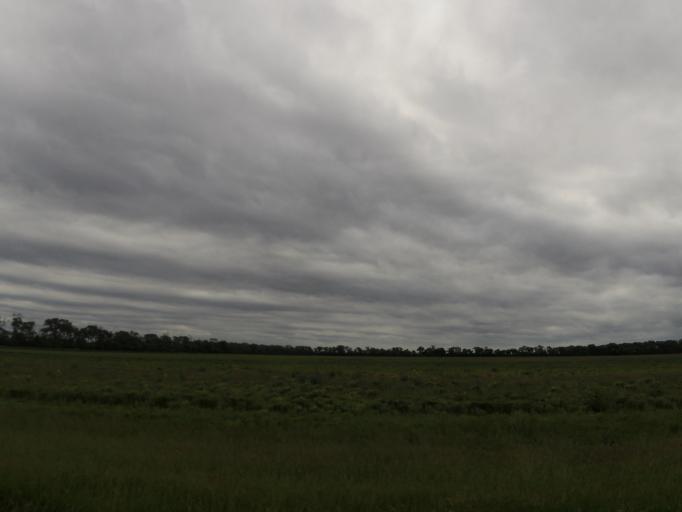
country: US
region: North Dakota
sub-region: Walsh County
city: Grafton
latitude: 48.5338
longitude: -97.4475
